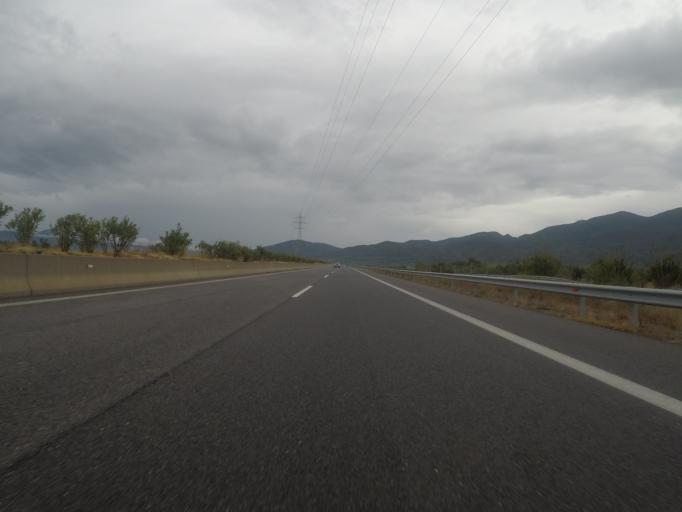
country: GR
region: Peloponnese
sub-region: Nomos Messinias
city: Meligalas
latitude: 37.2252
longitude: 22.0093
